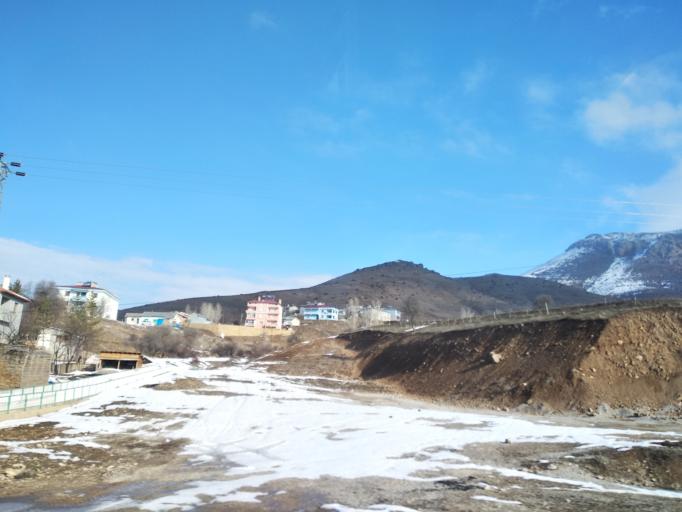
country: TR
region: Gumushane
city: Kelkit
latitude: 40.0129
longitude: 39.5284
